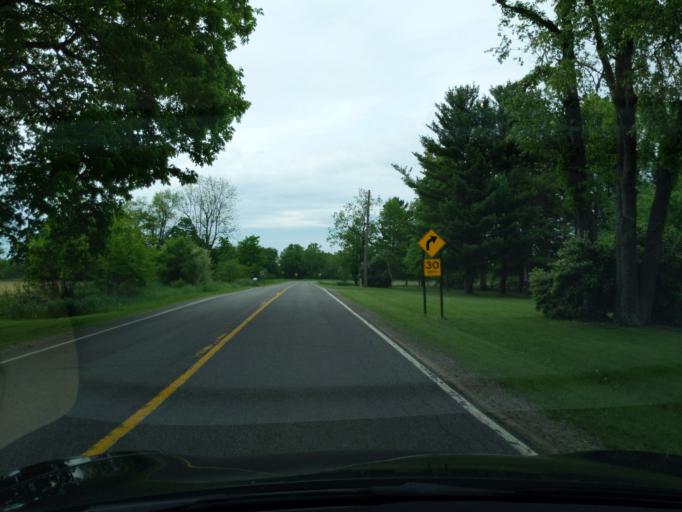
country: US
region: Michigan
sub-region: Ingham County
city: Leslie
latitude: 42.4524
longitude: -84.3561
